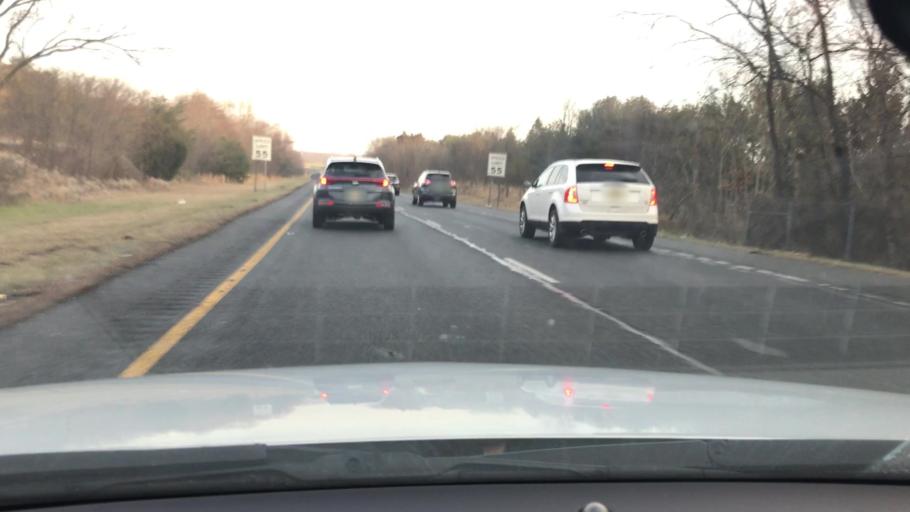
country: US
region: New Jersey
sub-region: Camden County
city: Glendora
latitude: 39.8229
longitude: -75.1044
